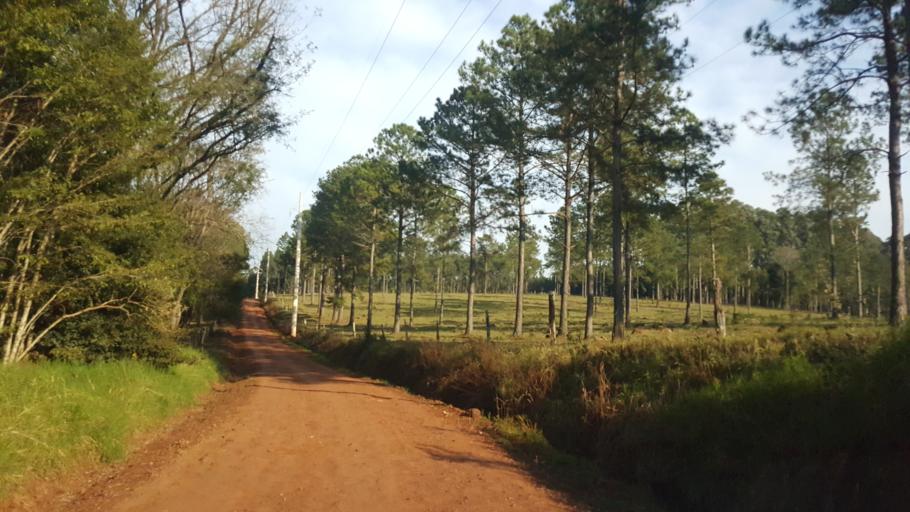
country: AR
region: Misiones
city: Capiovi
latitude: -26.9145
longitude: -55.0651
